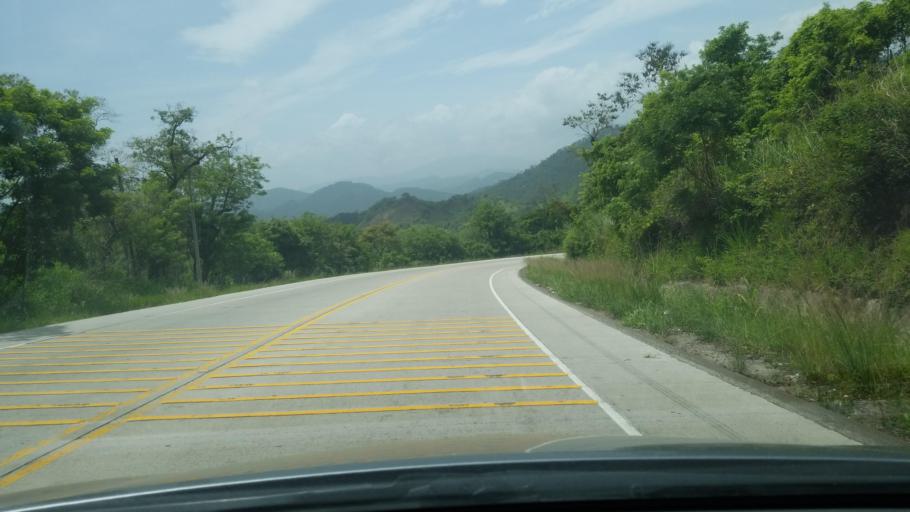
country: HN
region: Copan
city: Quezailica
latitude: 14.8997
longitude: -88.7568
